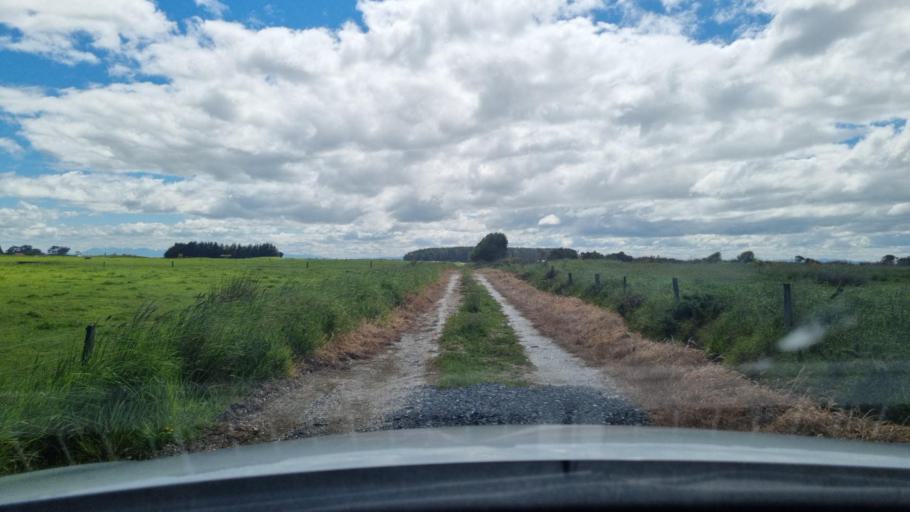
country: NZ
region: Southland
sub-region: Invercargill City
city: Invercargill
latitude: -46.4184
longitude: 168.2709
